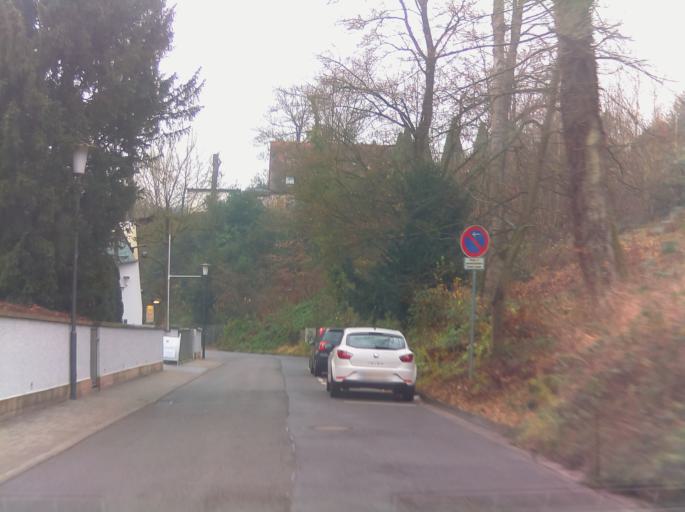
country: DE
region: Baden-Wuerttemberg
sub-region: Karlsruhe Region
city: Heidelberg
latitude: 49.4154
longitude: 8.7345
